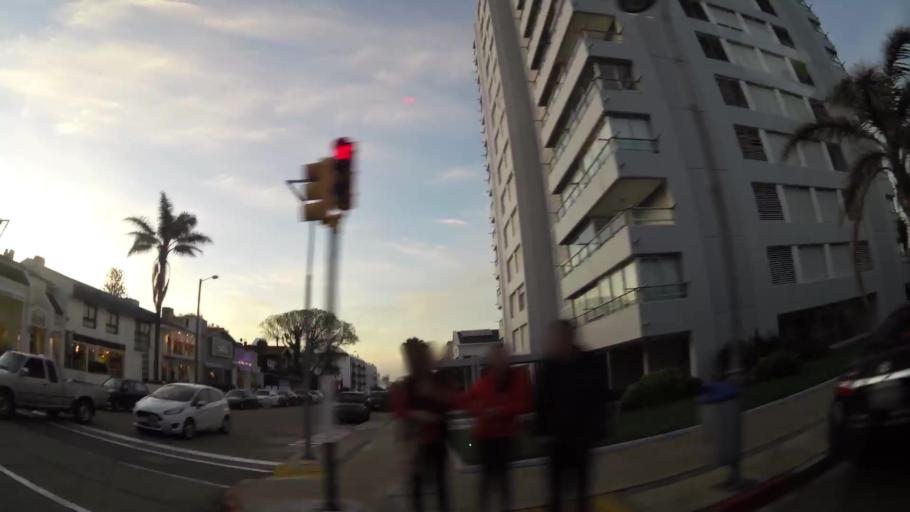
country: UY
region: Maldonado
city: Punta del Este
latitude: -34.9593
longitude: -54.9421
